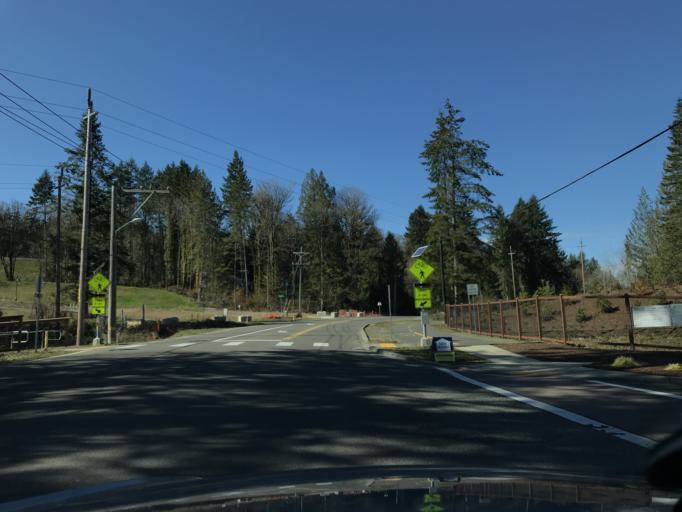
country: US
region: Washington
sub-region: Pierce County
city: Canterwood
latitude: 47.3490
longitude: -122.6054
